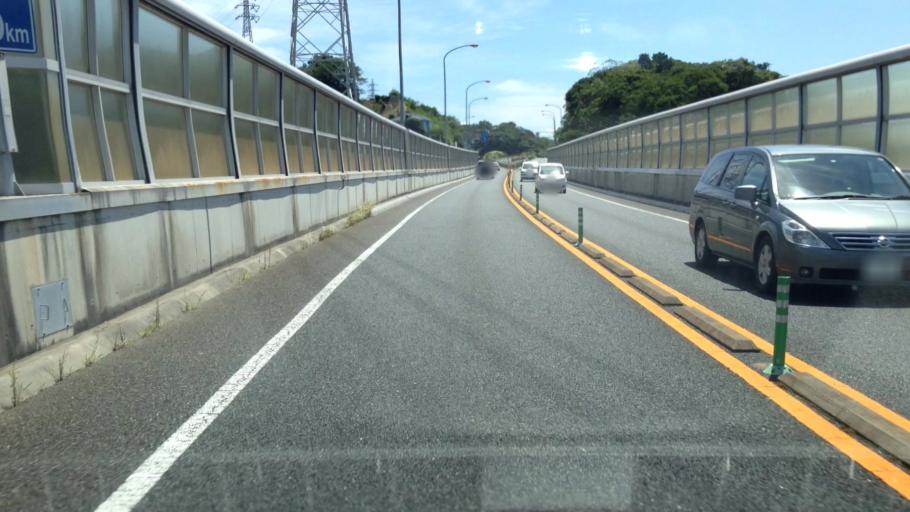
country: JP
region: Kanagawa
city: Yokosuka
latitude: 35.2171
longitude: 139.6375
